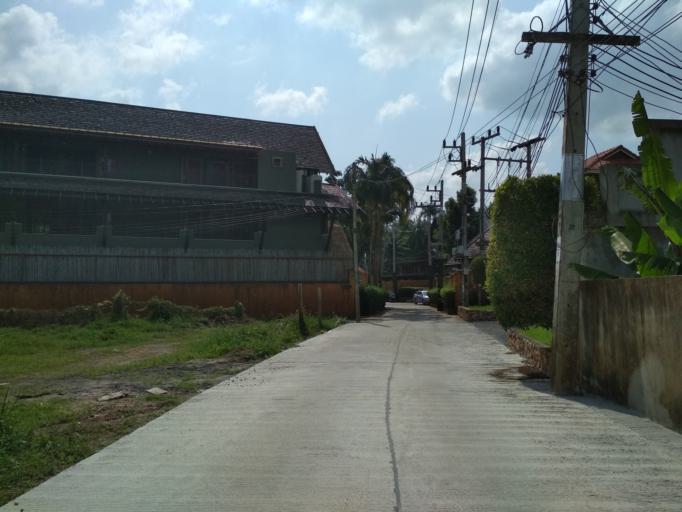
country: TH
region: Surat Thani
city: Ko Samui
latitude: 9.5701
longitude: 99.9180
